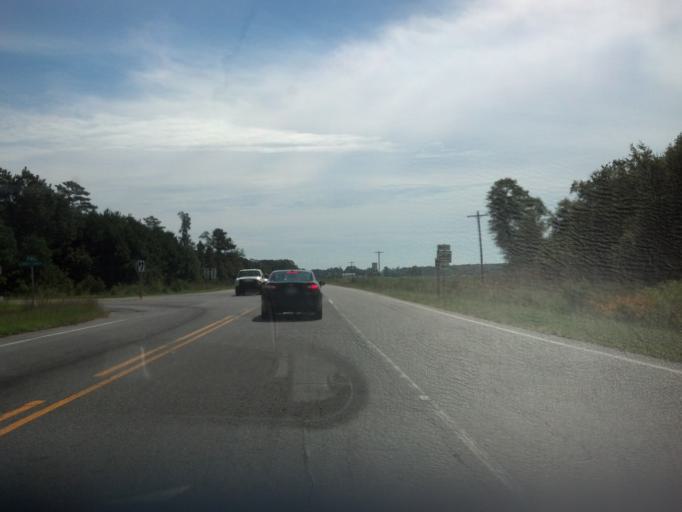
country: US
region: North Carolina
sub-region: Pitt County
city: Farmville
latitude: 35.5781
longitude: -77.5869
